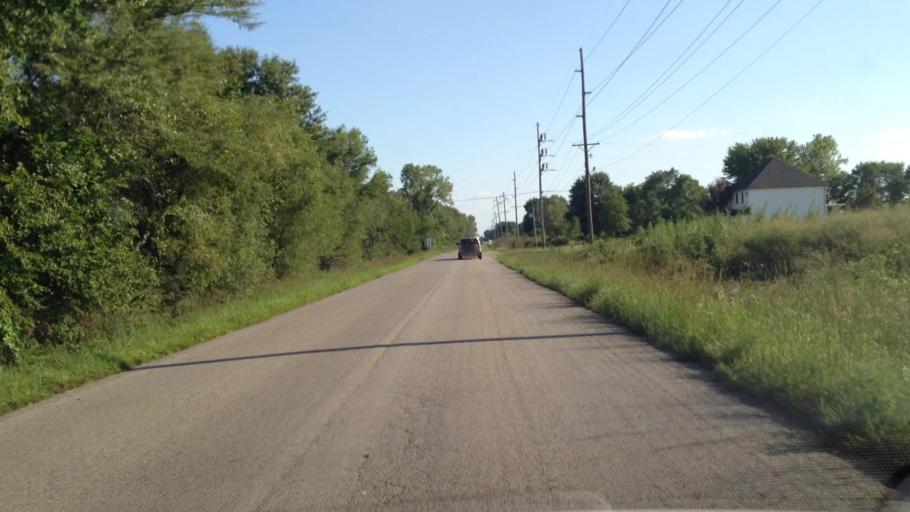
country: US
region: Kansas
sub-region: Crawford County
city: Frontenac
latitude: 37.4562
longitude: -94.6308
